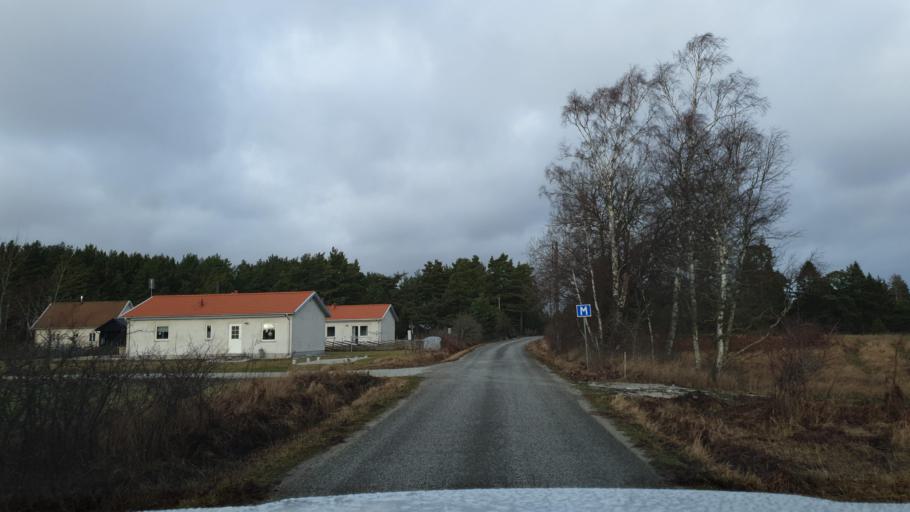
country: SE
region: Gotland
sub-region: Gotland
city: Slite
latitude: 57.3848
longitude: 18.8085
